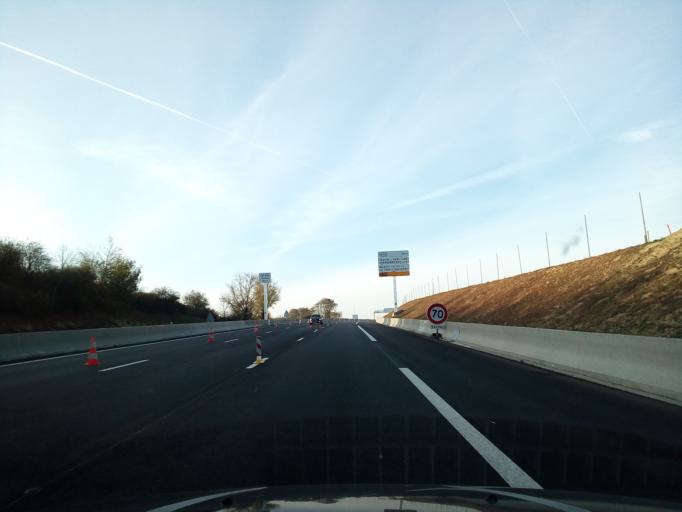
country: FR
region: Rhone-Alpes
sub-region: Departement du Rhone
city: Dardilly
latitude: 45.8280
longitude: 4.7398
